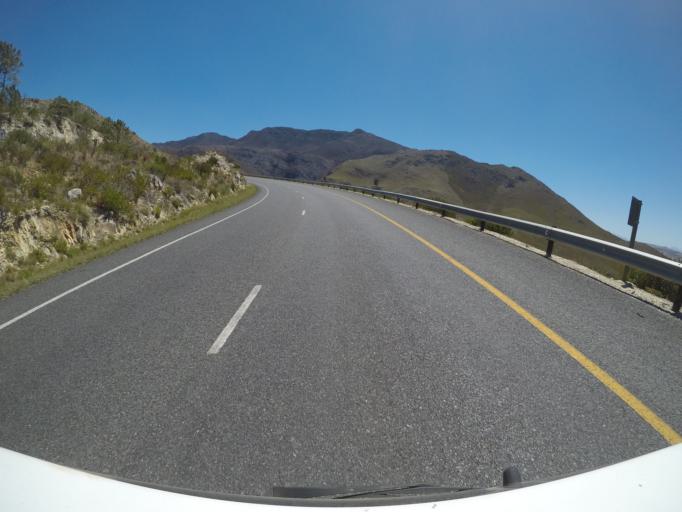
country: ZA
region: Western Cape
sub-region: Overberg District Municipality
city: Grabouw
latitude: -34.2193
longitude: 19.1896
